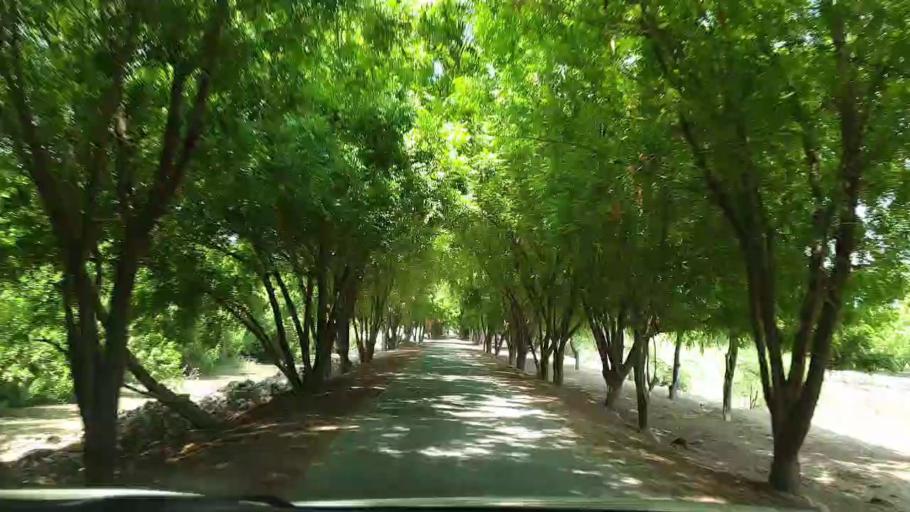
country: PK
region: Sindh
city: Dokri
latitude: 27.3593
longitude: 68.1136
